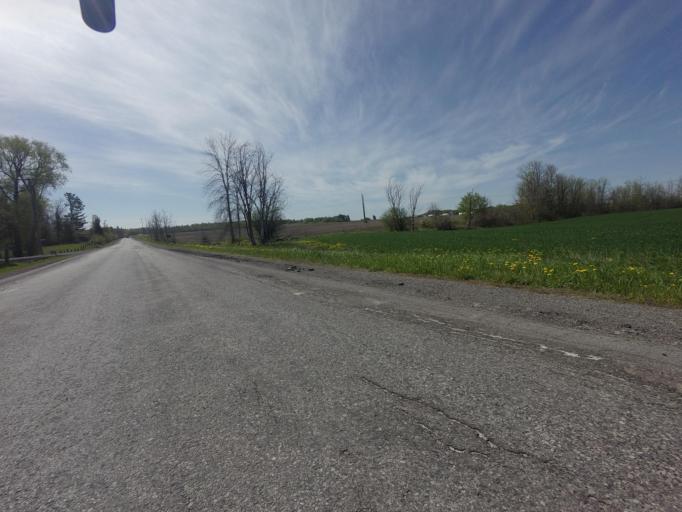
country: CA
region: Ontario
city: Arnprior
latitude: 45.4141
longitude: -76.2178
